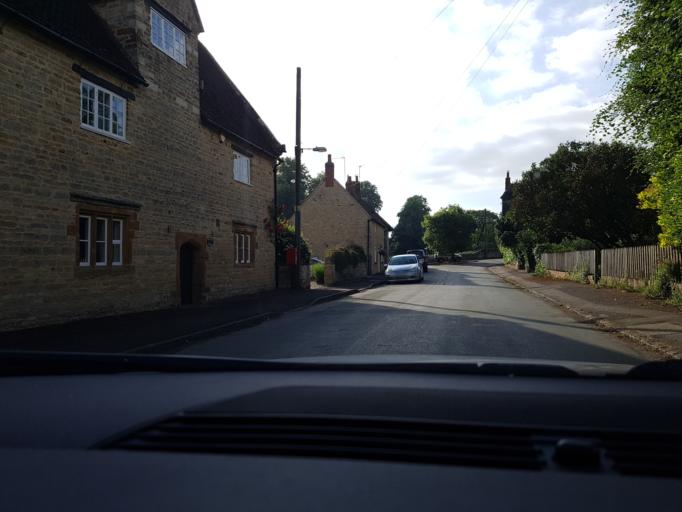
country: GB
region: England
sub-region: Northamptonshire
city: Deanshanger
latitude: 52.0476
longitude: -0.9136
